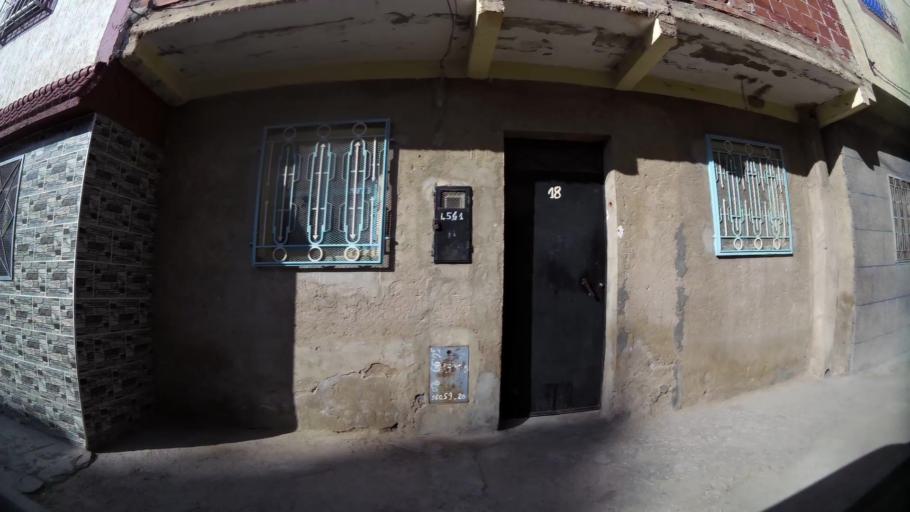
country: MA
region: Oriental
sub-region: Oujda-Angad
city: Oujda
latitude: 34.7106
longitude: -1.8909
